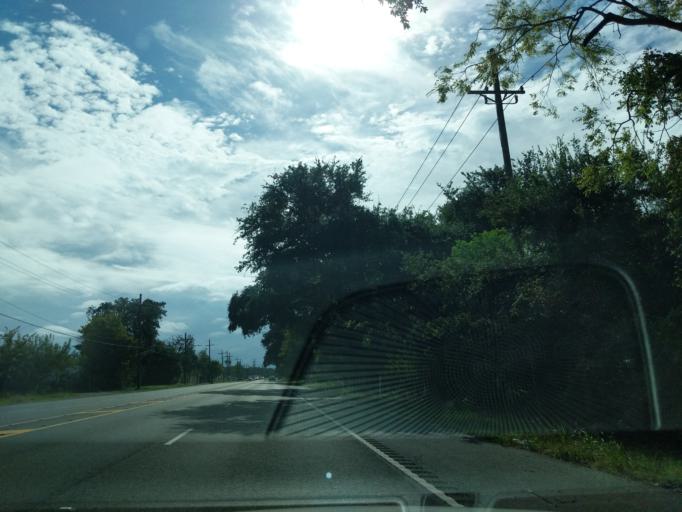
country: US
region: Louisiana
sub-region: Saint Bernard Parish
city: Chalmette
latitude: 30.0450
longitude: -89.8921
